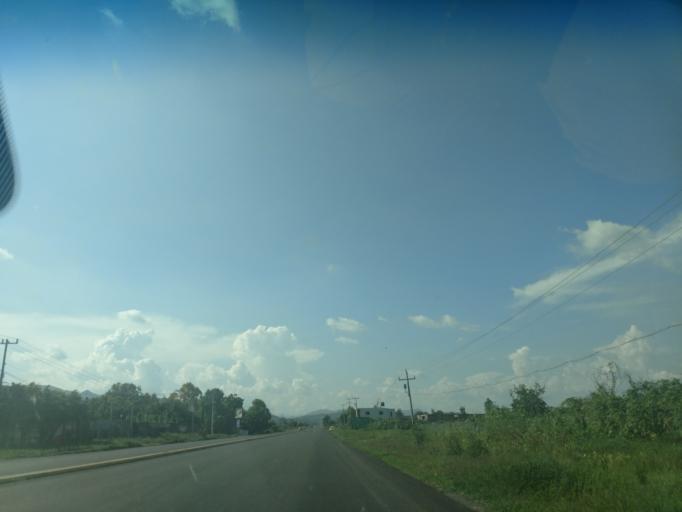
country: MX
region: Jalisco
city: Ahualulco de Mercado
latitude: 20.7103
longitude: -103.9741
